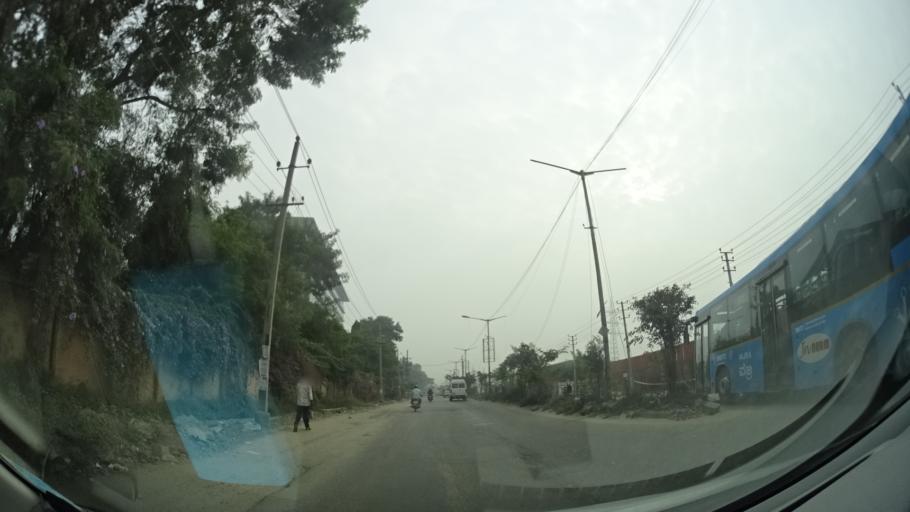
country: IN
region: Karnataka
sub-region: Bangalore Urban
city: Bangalore
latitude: 12.9932
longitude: 77.7068
